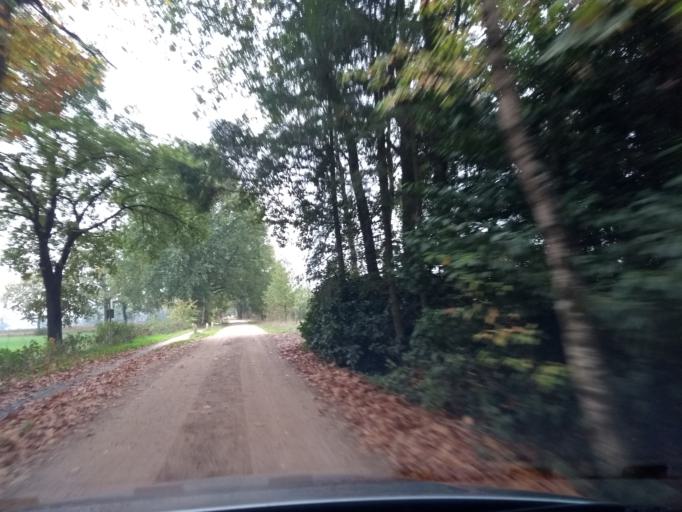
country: NL
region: Gelderland
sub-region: Gemeente Bronckhorst
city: Zelhem
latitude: 52.0438
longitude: 6.3584
